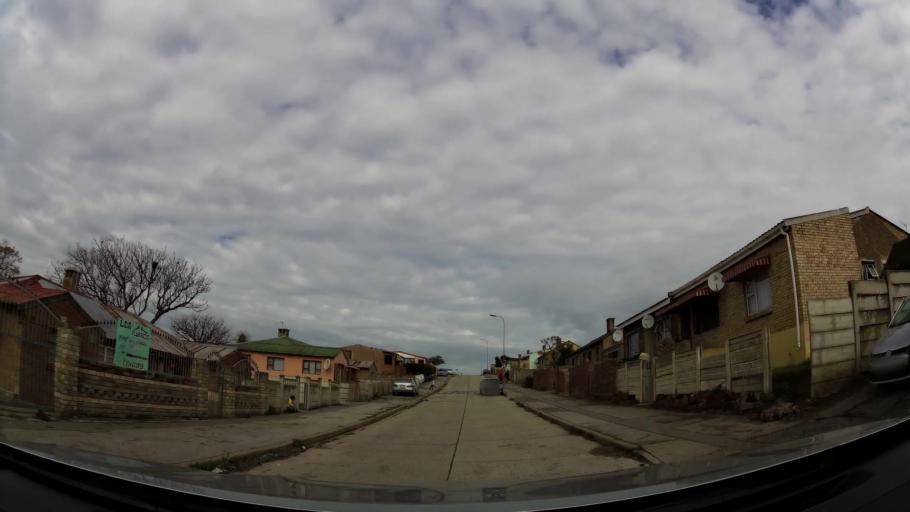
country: ZA
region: Eastern Cape
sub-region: Nelson Mandela Bay Metropolitan Municipality
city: Port Elizabeth
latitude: -33.9364
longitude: 25.5758
